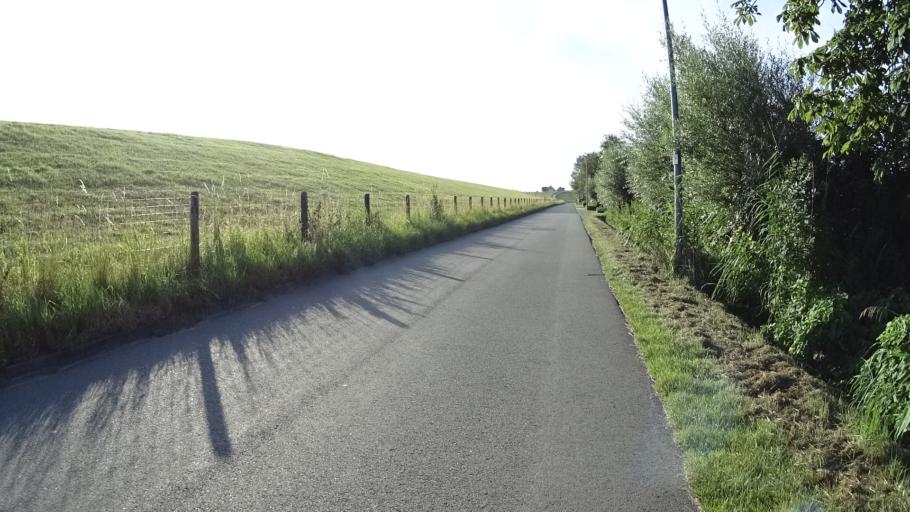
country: DE
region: Lower Saxony
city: Butjadingen
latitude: 53.6007
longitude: 8.3492
